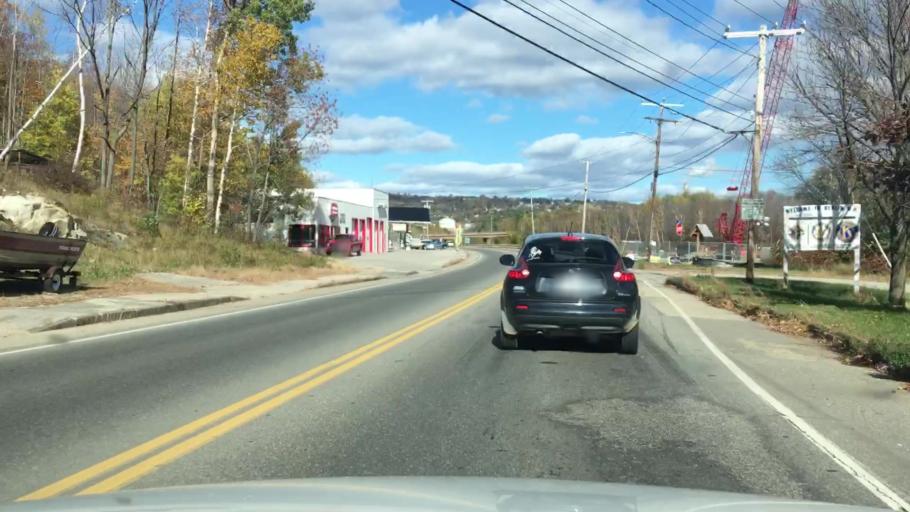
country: US
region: New Hampshire
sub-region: Coos County
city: Berlin
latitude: 44.4558
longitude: -71.1878
